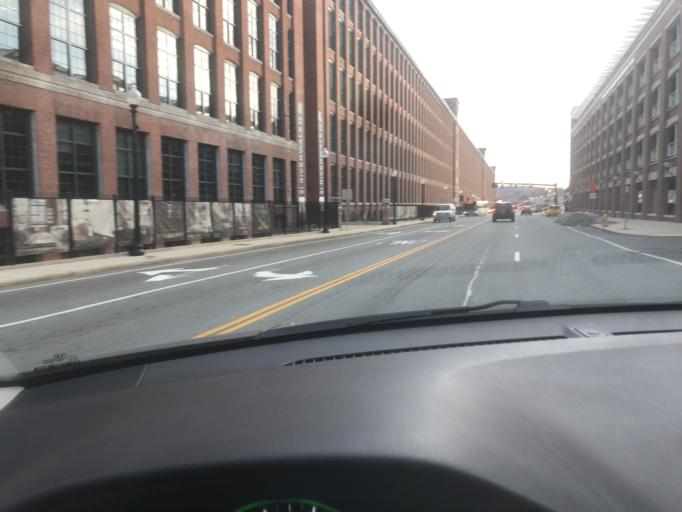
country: US
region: Massachusetts
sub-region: Essex County
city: Lawrence
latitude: 42.7024
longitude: -71.1533
